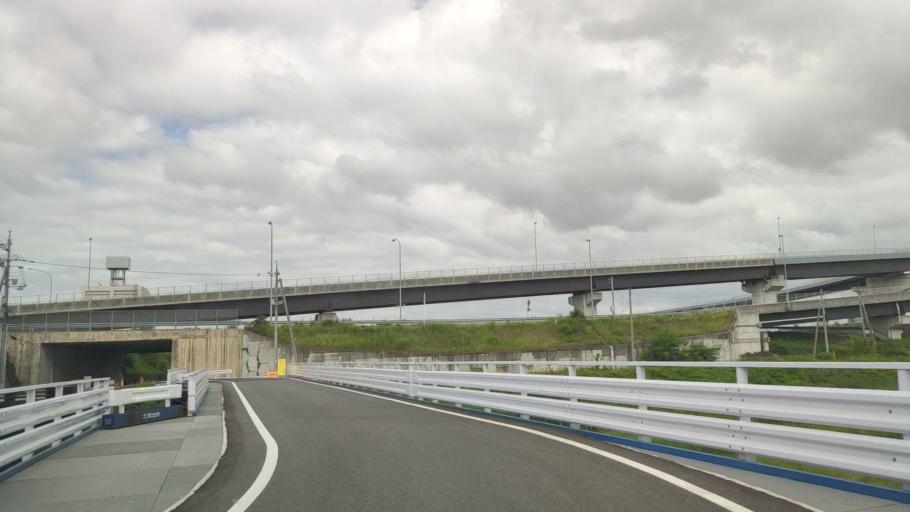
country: JP
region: Tottori
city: Yonago
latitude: 35.4240
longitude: 133.4011
